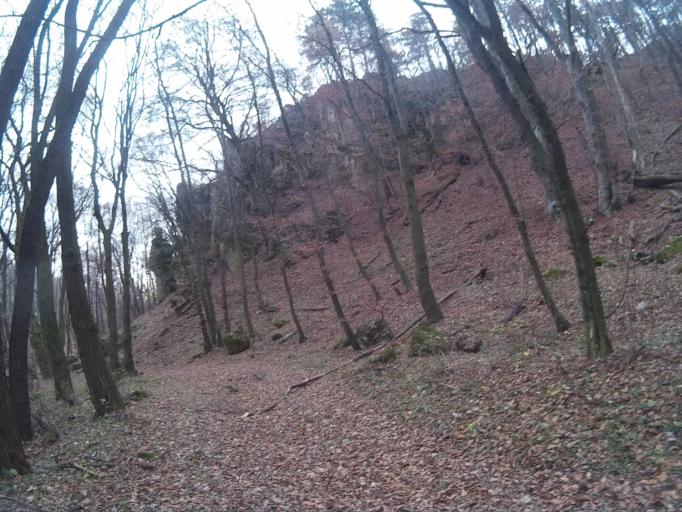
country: HU
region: Veszprem
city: Tapolca
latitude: 46.9457
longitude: 17.4945
